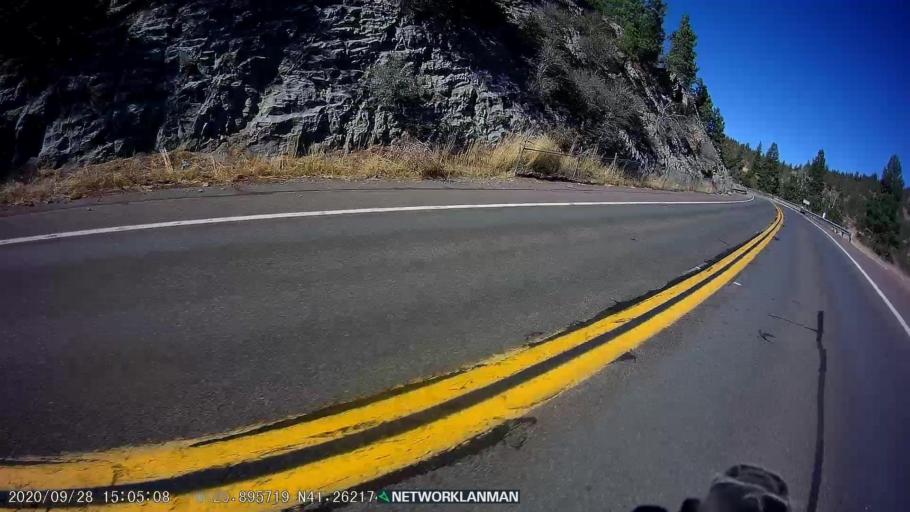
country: US
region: California
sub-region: Modoc County
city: Alturas
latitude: 41.2638
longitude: -120.8945
